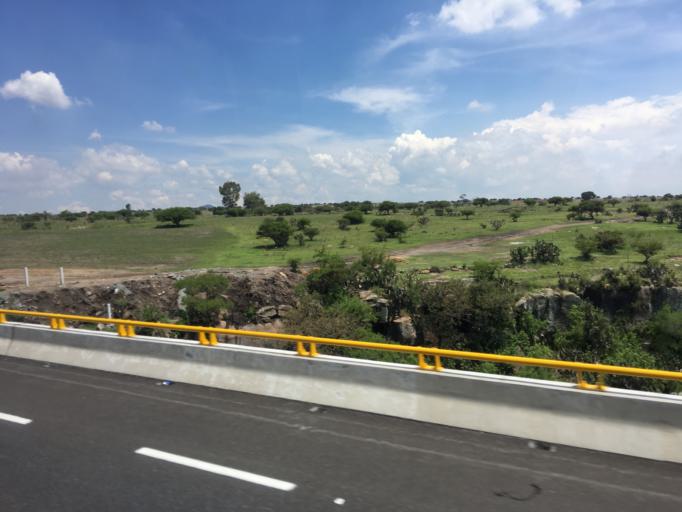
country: MX
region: Mexico
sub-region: Aculco
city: San Pedro Denxhi Centro
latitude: 20.2688
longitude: -100.0160
